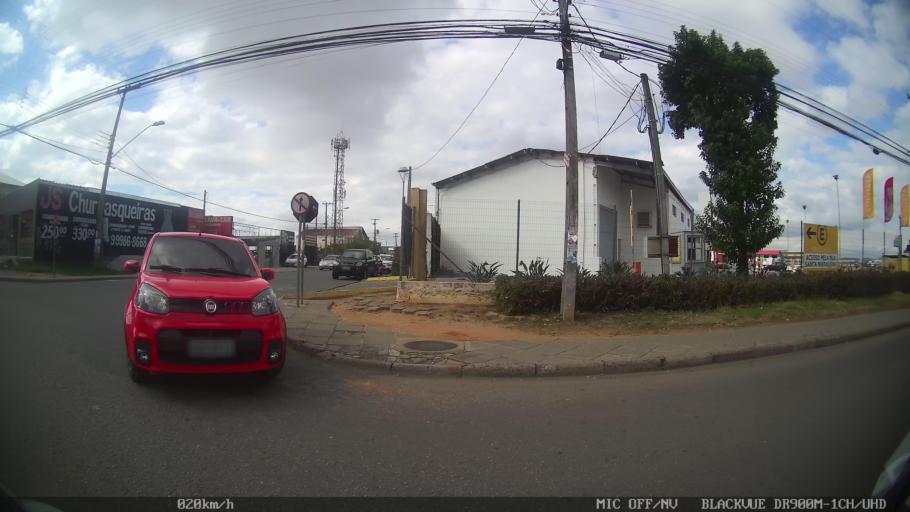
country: BR
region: Parana
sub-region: Colombo
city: Colombo
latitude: -25.3623
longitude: -49.1858
